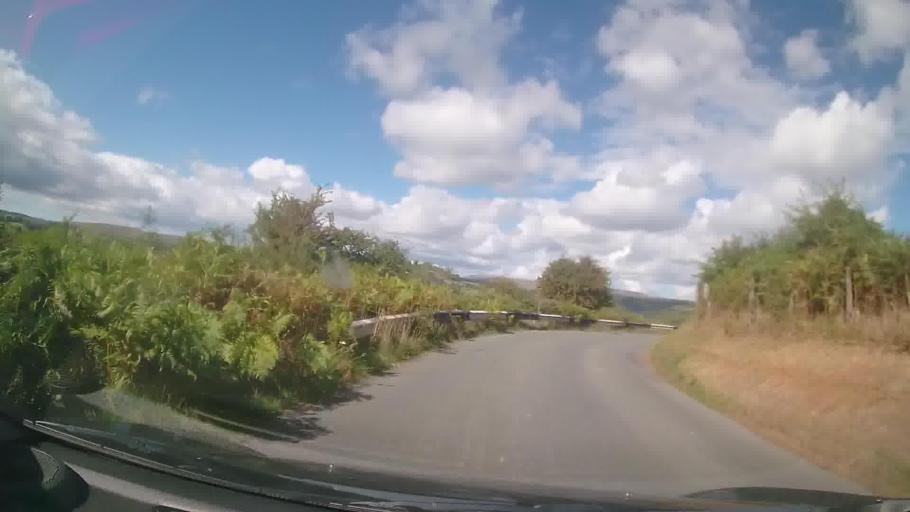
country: GB
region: Wales
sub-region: Merthyr Tydfil County Borough
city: Merthyr Tydfil
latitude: 51.7794
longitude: -3.3657
